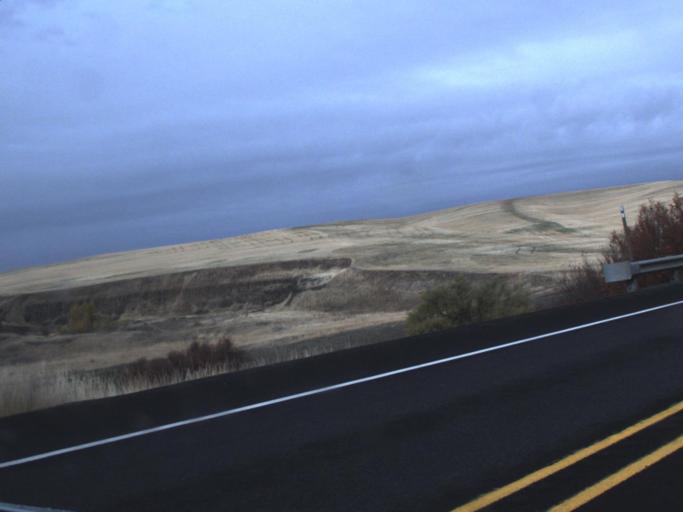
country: US
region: Washington
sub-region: Whitman County
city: Pullman
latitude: 46.5955
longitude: -117.1734
